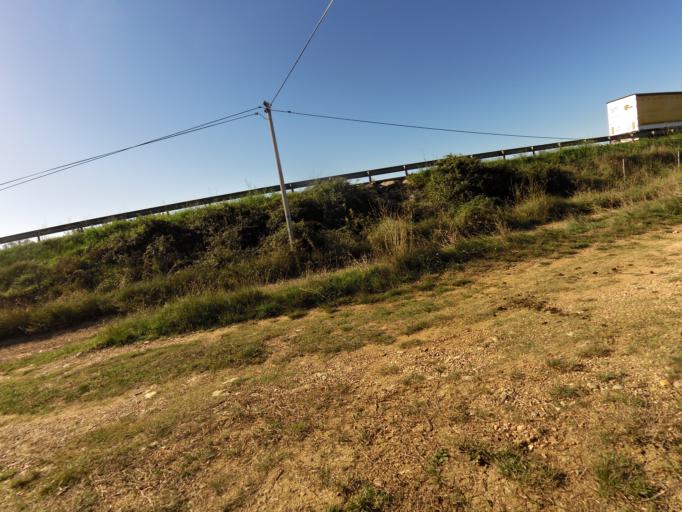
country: FR
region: Languedoc-Roussillon
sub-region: Departement du Gard
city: Gallargues-le-Montueux
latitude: 43.7247
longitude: 4.1619
